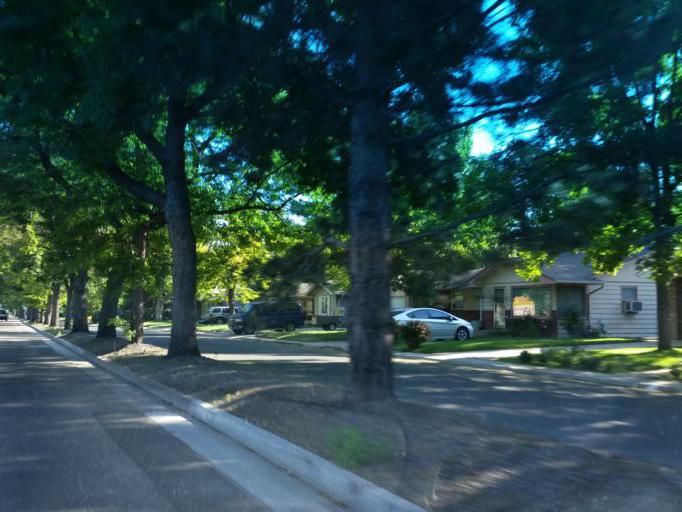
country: US
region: Colorado
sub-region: Larimer County
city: Fort Collins
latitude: 40.5544
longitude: -105.0770
